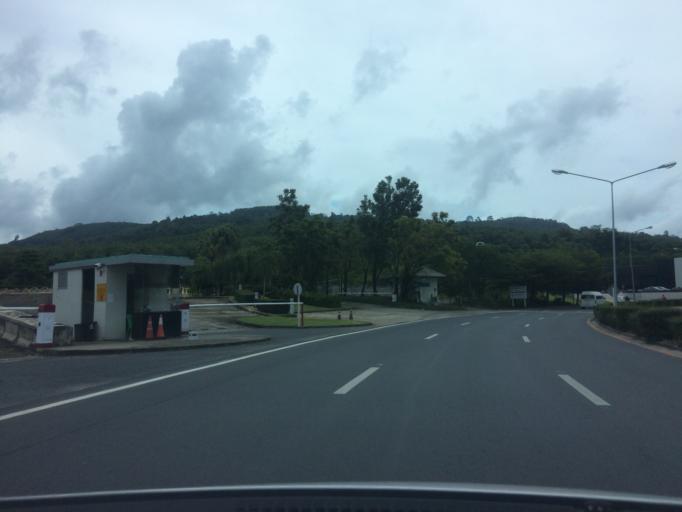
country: TH
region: Phuket
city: Mueang Phuket
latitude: 7.8691
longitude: 98.3569
